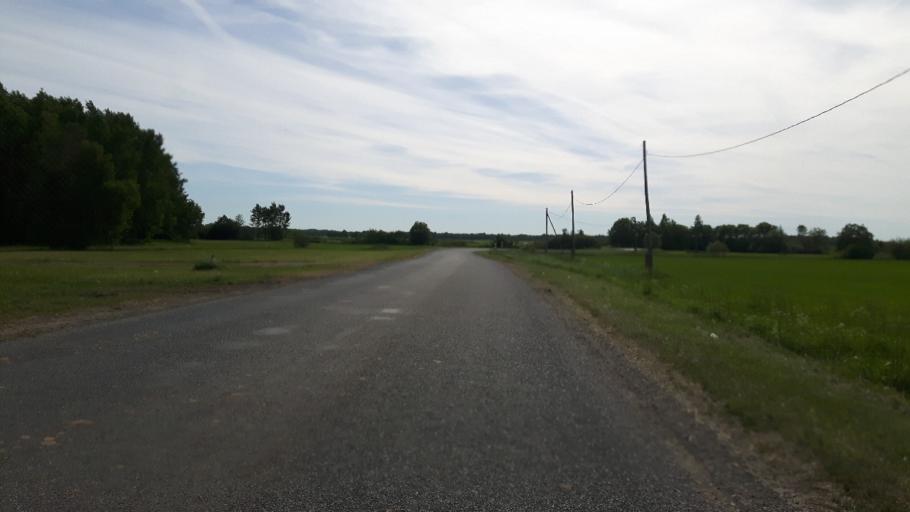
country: EE
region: Harju
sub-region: Raasiku vald
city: Arukula
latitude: 59.4235
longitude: 25.0855
